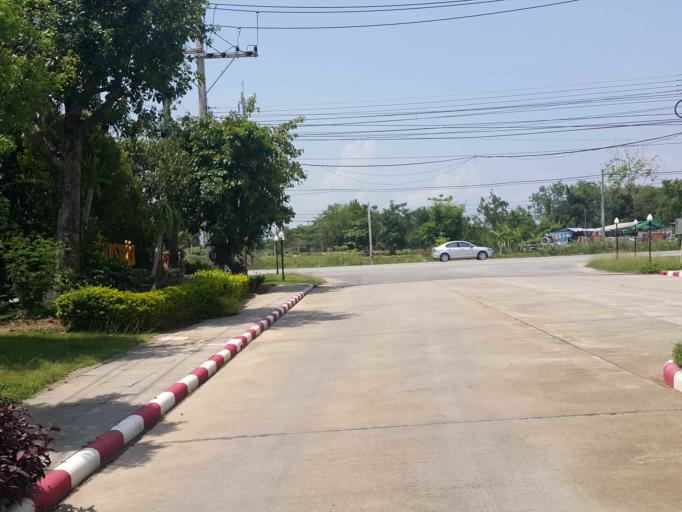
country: TH
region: Chiang Mai
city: San Sai
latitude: 18.8361
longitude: 99.0311
